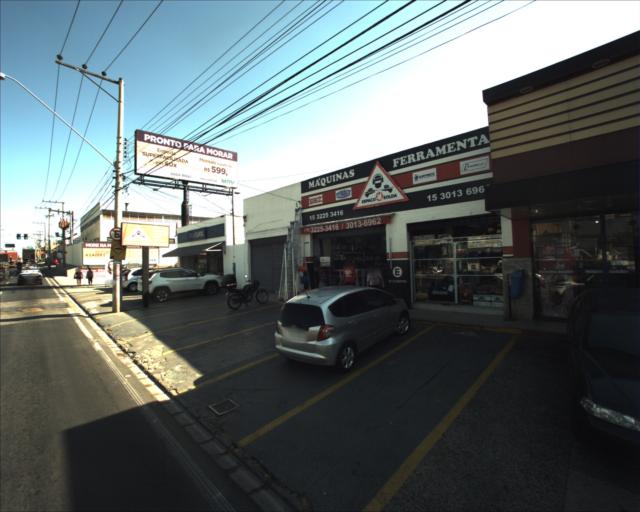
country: BR
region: Sao Paulo
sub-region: Sorocaba
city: Sorocaba
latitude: -23.4228
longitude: -47.4127
